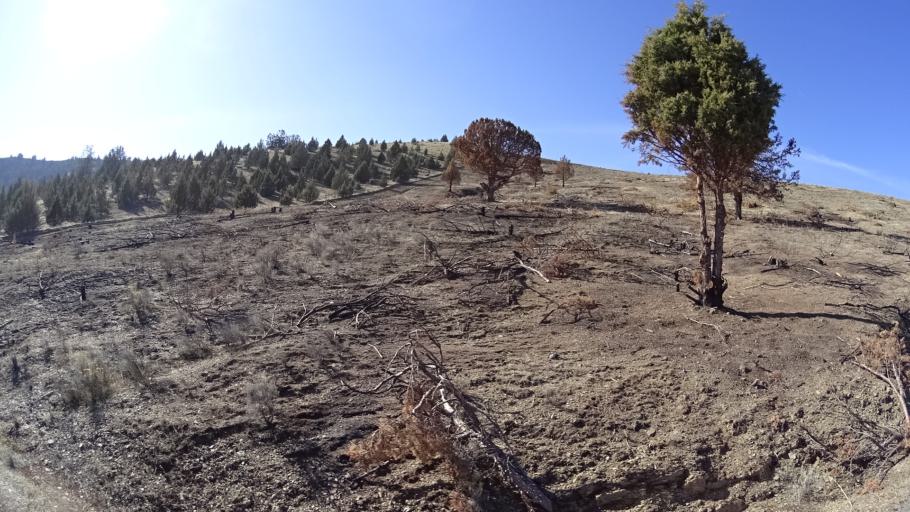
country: US
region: California
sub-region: Siskiyou County
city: Montague
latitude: 41.6332
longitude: -122.5400
